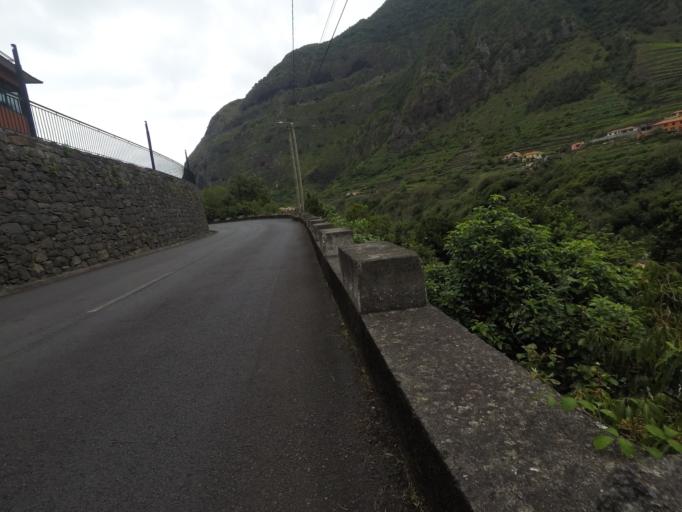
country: PT
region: Madeira
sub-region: Sao Vicente
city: Sao Vicente
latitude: 32.7984
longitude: -17.0437
